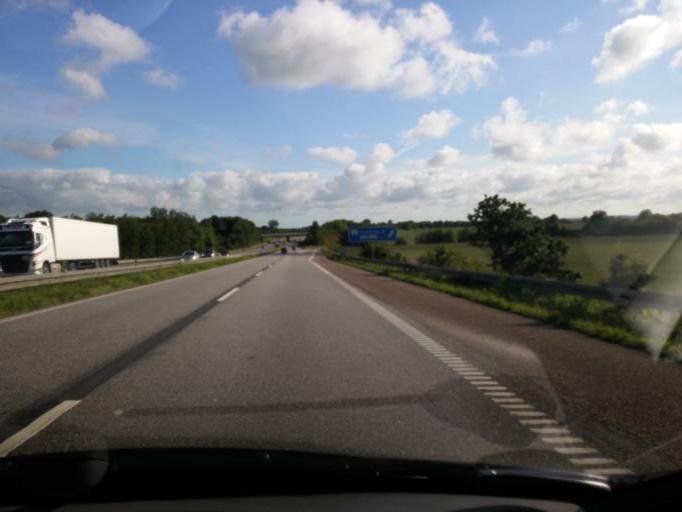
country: DK
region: Zealand
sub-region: Slagelse Kommune
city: Slagelse
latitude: 55.4139
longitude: 11.4118
